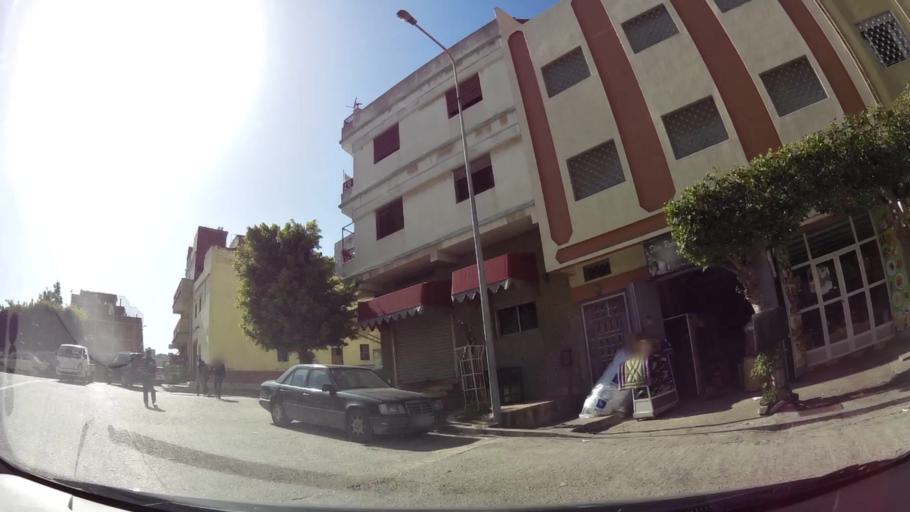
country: MA
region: Tanger-Tetouan
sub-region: Tanger-Assilah
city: Tangier
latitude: 35.7470
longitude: -5.8053
